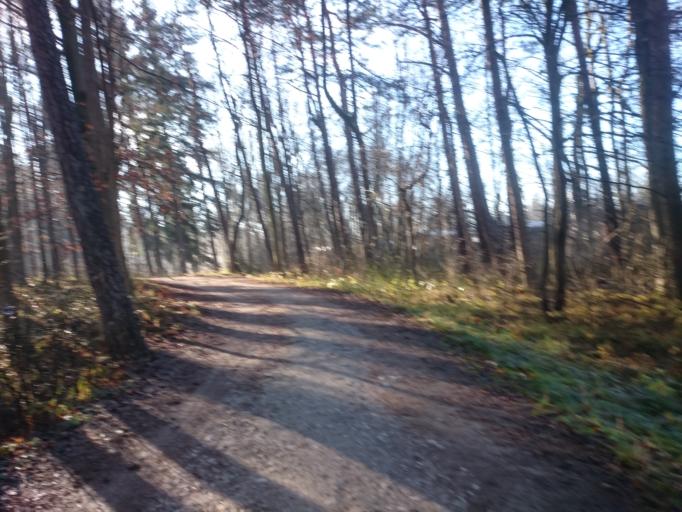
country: DE
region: Bavaria
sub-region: Swabia
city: Konigsbrunn
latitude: 48.3011
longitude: 10.9110
